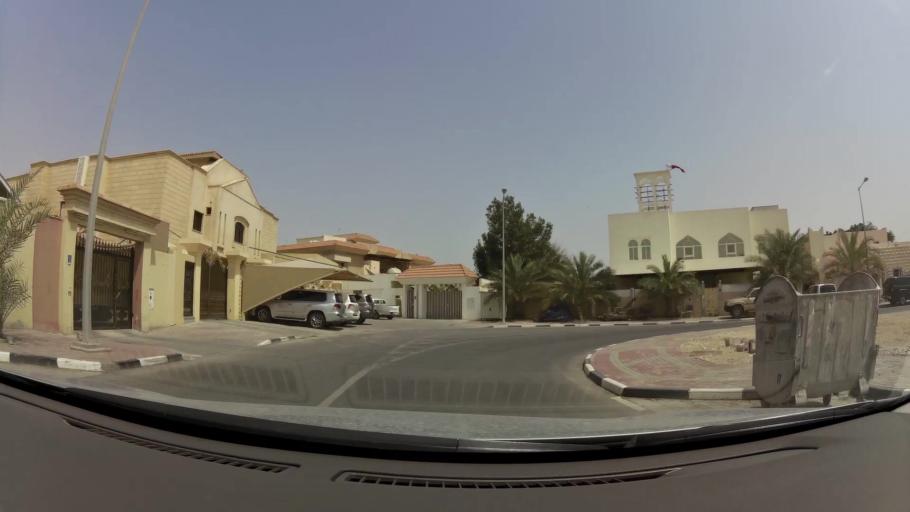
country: QA
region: Baladiyat ar Rayyan
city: Ar Rayyan
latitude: 25.2488
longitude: 51.4269
